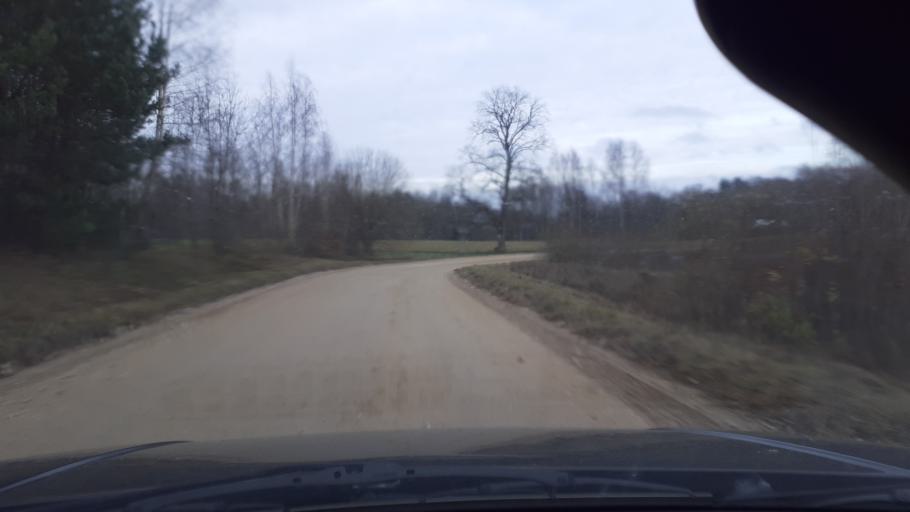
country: LV
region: Alsunga
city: Alsunga
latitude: 56.9456
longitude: 21.6368
